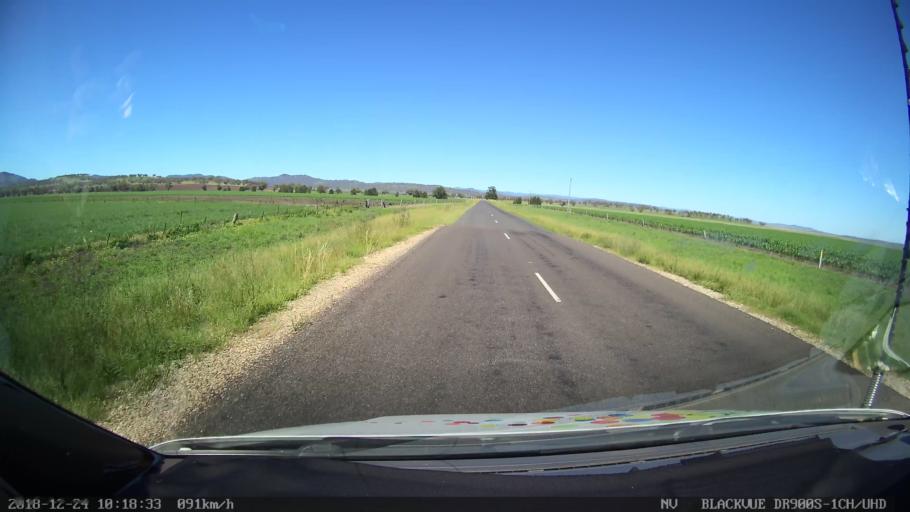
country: AU
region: New South Wales
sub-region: Liverpool Plains
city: Quirindi
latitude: -31.7242
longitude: 150.5748
